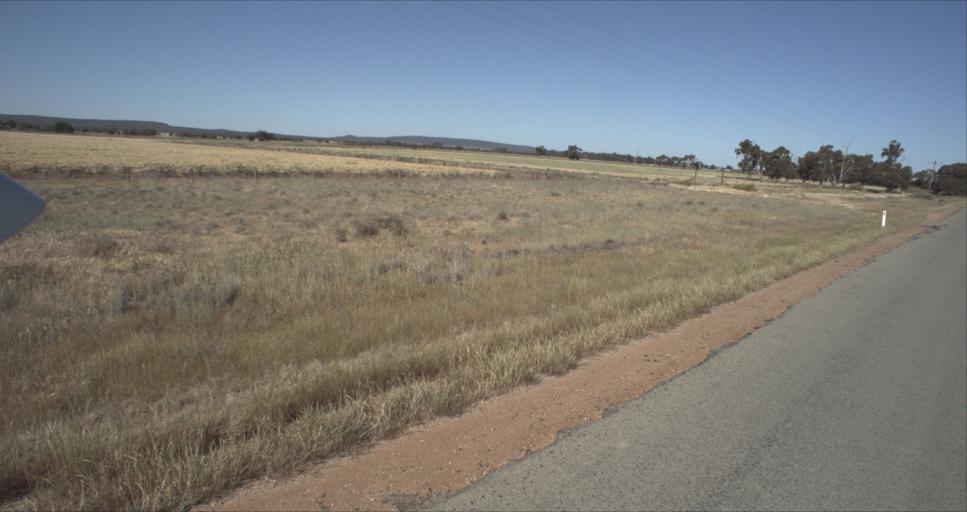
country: AU
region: New South Wales
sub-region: Leeton
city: Leeton
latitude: -34.4979
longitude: 146.3915
